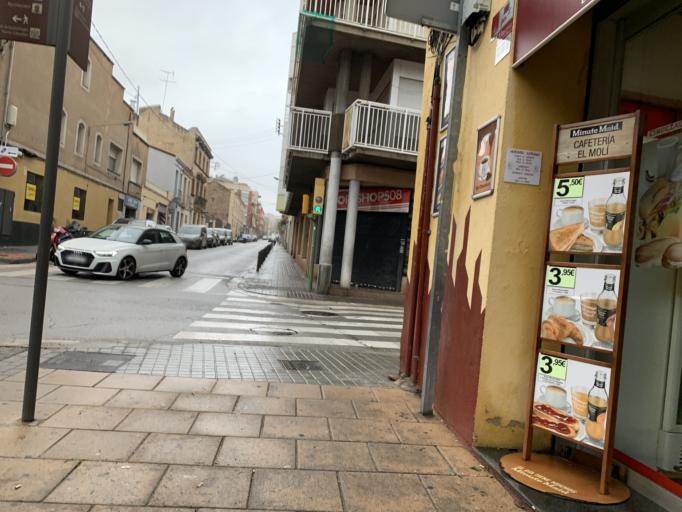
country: ES
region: Catalonia
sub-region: Provincia de Barcelona
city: Mataro
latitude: 41.5351
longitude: 2.4414
